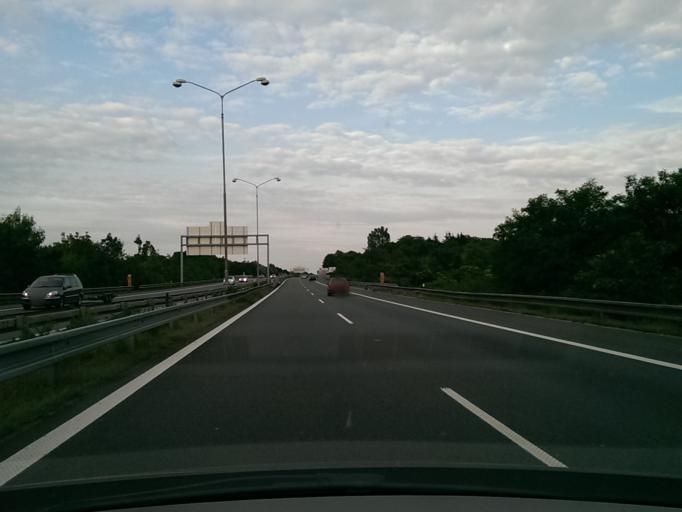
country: CZ
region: South Moravian
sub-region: Mesto Brno
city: Brno
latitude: 49.1612
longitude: 16.6444
